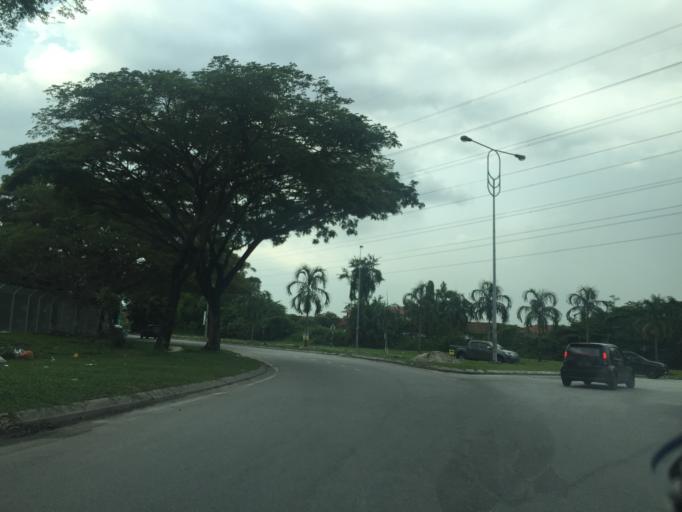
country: MY
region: Selangor
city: Klang
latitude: 2.9905
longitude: 101.4433
